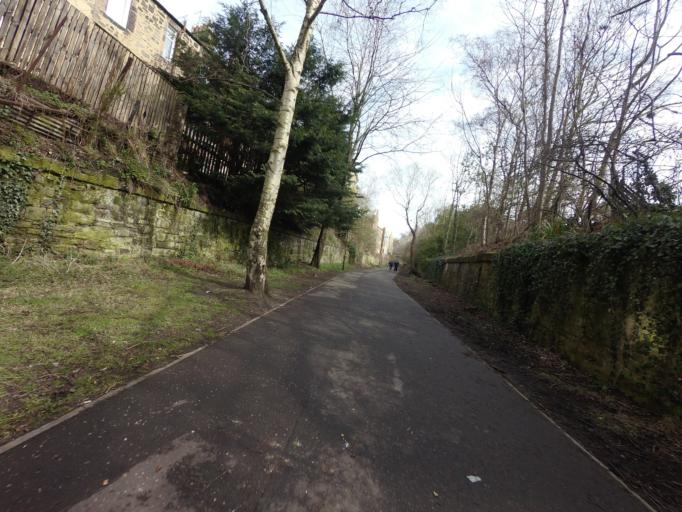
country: GB
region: Scotland
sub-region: Edinburgh
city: Edinburgh
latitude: 55.9731
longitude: -3.1852
